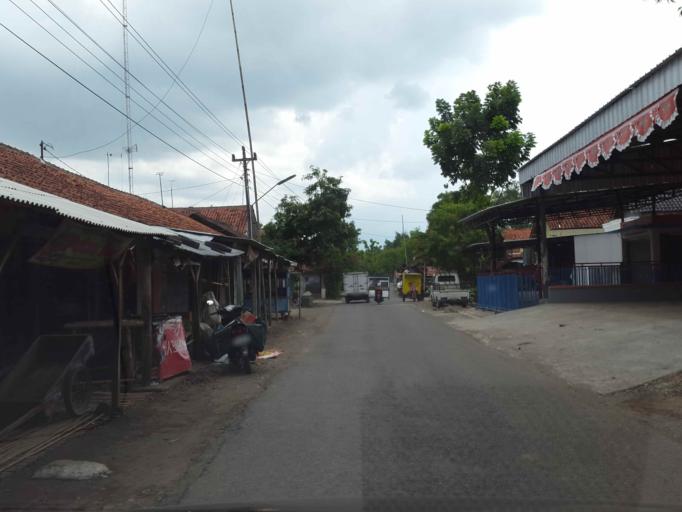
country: ID
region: Central Java
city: Ketanggungan
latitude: -6.9808
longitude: 108.8803
